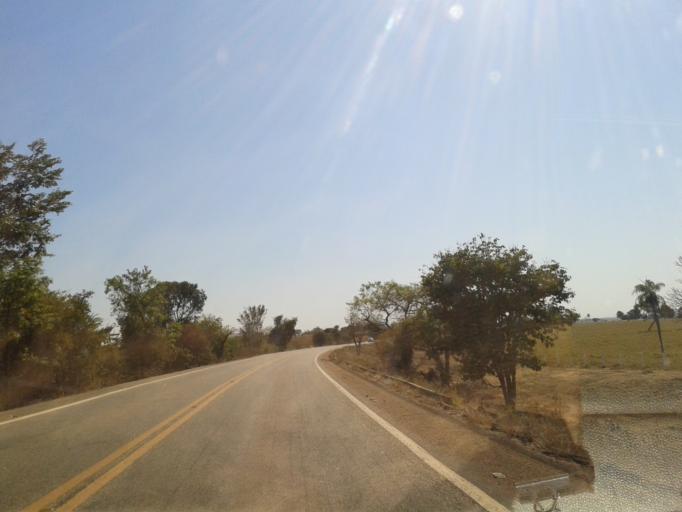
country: BR
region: Goias
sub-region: Crixas
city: Crixas
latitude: -14.2034
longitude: -50.3899
